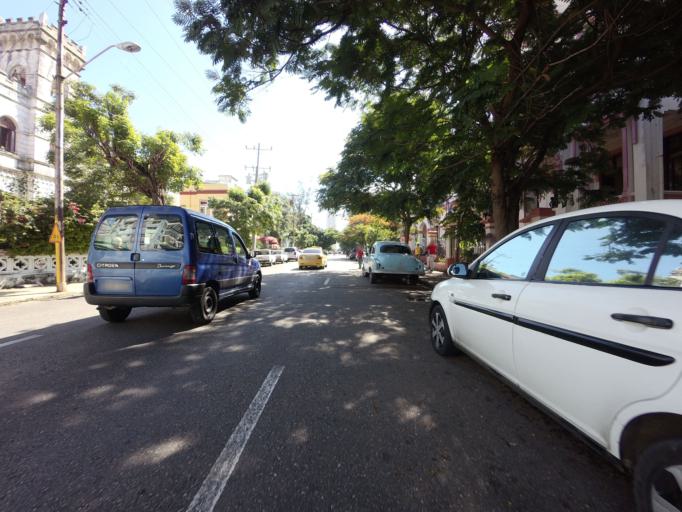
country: CU
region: La Habana
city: Havana
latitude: 23.1406
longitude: -82.3880
